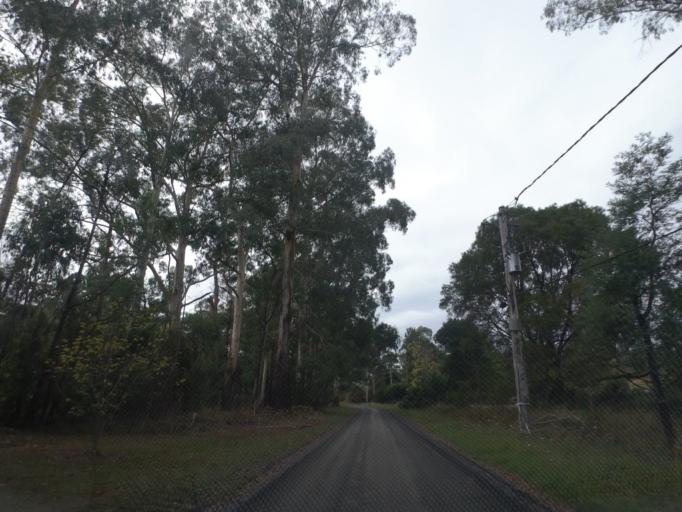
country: AU
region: Victoria
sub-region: Yarra Ranges
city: Healesville
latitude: -37.6409
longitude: 145.5319
